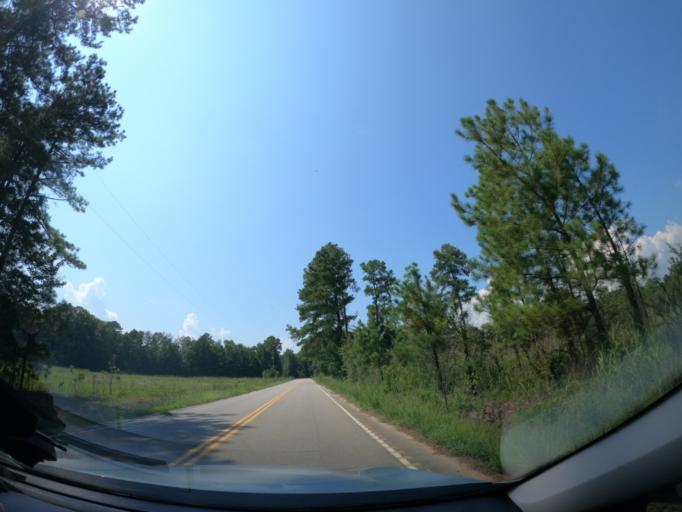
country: US
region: South Carolina
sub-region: Richland County
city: Hopkins
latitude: 33.8623
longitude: -80.8824
